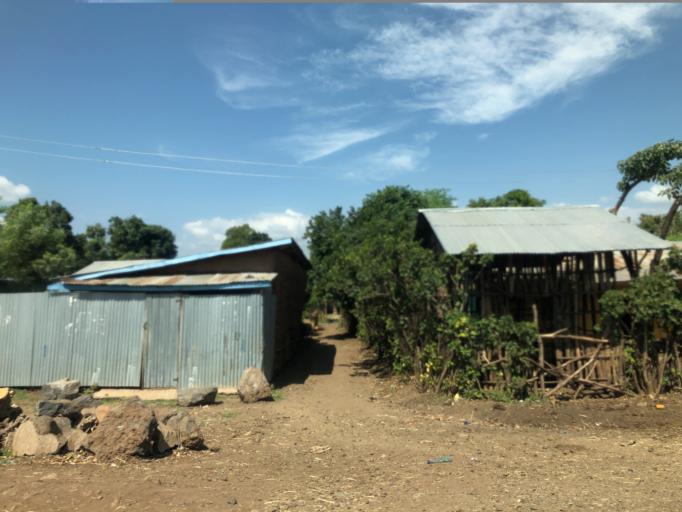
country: ET
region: Southern Nations, Nationalities, and People's Region
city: Arba Minch'
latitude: 5.8409
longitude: 37.4620
